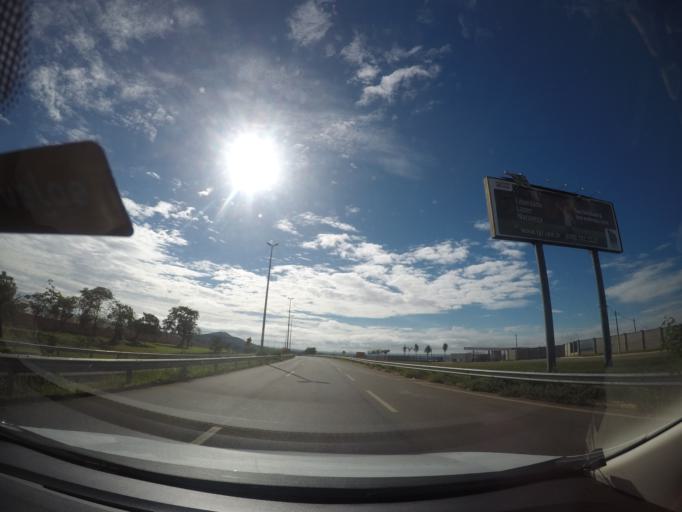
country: BR
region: Goias
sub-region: Senador Canedo
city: Senador Canedo
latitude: -16.6867
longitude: -49.1541
